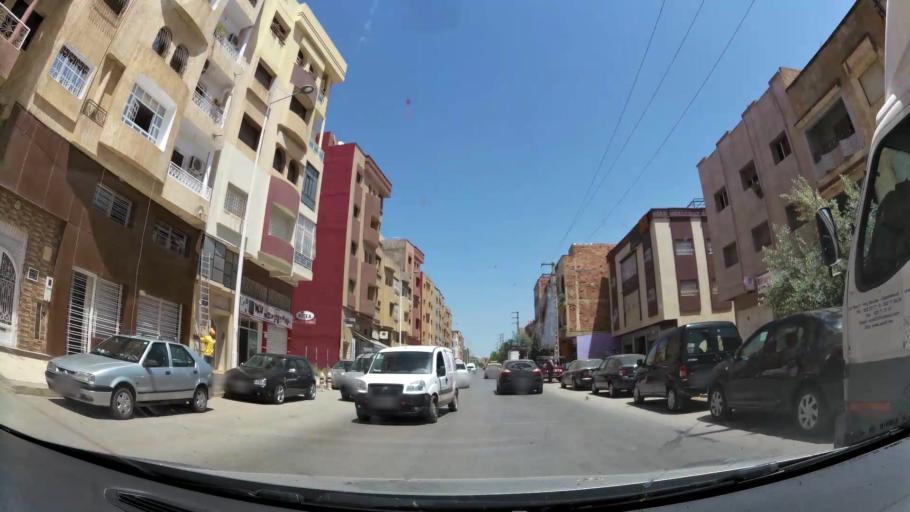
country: MA
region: Rabat-Sale-Zemmour-Zaer
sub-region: Khemisset
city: Khemisset
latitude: 33.8271
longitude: -6.0774
